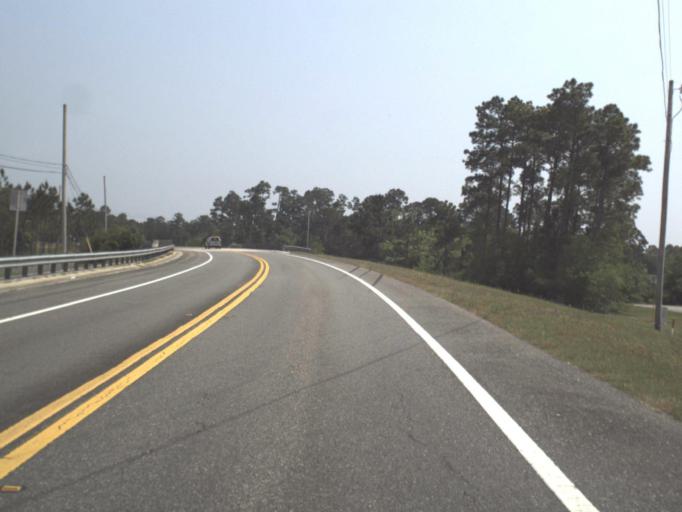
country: US
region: Florida
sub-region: Santa Rosa County
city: Bagdad
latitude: 30.5154
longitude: -87.0872
